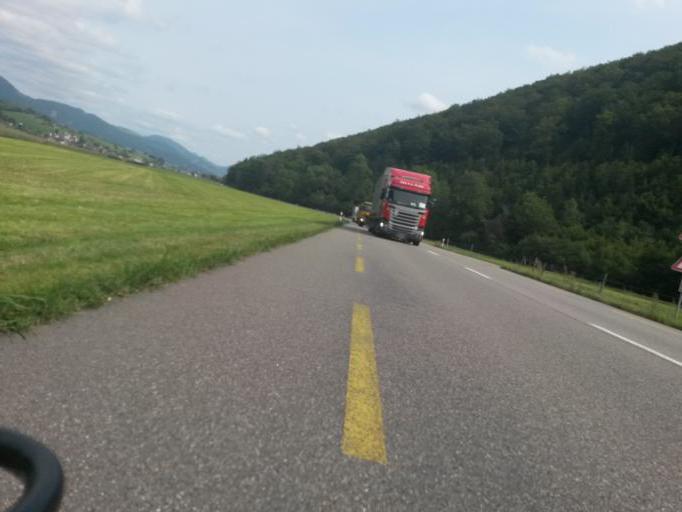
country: CH
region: Solothurn
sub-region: Bezirk Thal
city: Welschenrohr
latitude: 47.2873
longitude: 7.5712
